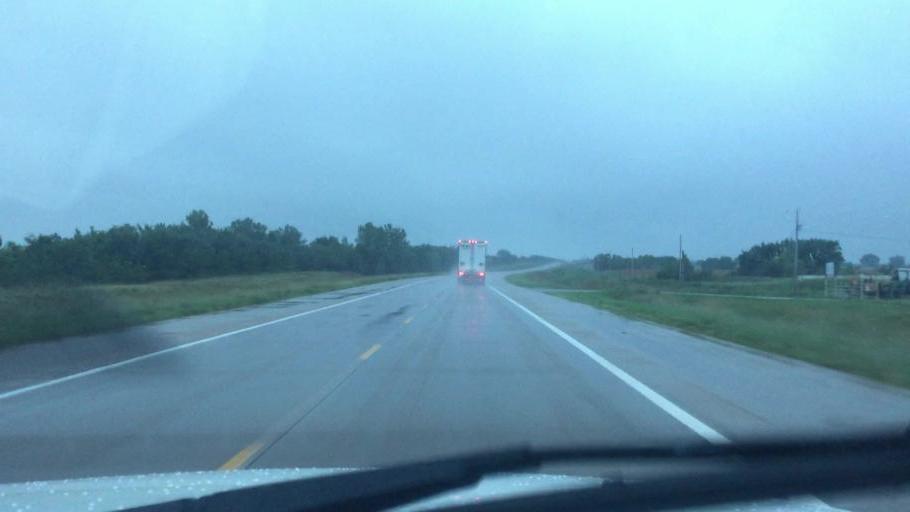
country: US
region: Kansas
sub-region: Neosho County
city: Chanute
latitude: 37.5236
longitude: -95.4713
